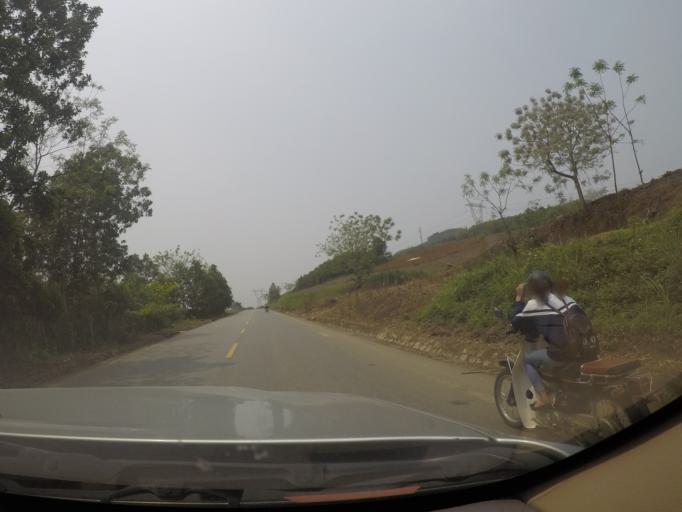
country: VN
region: Thanh Hoa
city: Thi Tran Cam Thuy
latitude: 20.1632
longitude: 105.4718
